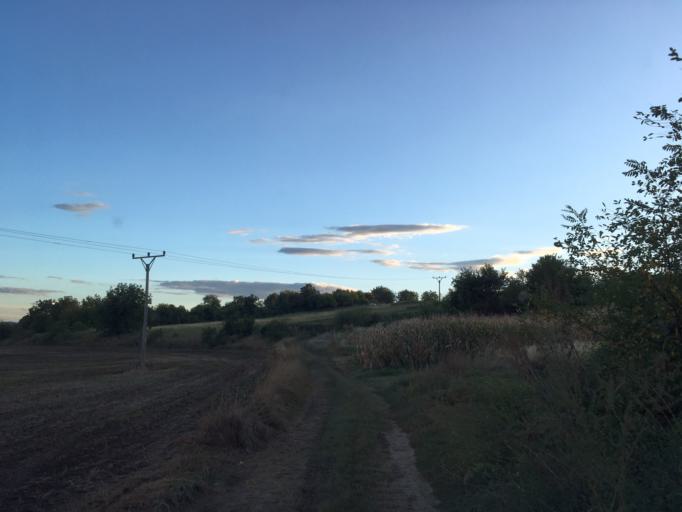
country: SK
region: Nitriansky
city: Svodin
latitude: 47.9108
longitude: 18.4417
